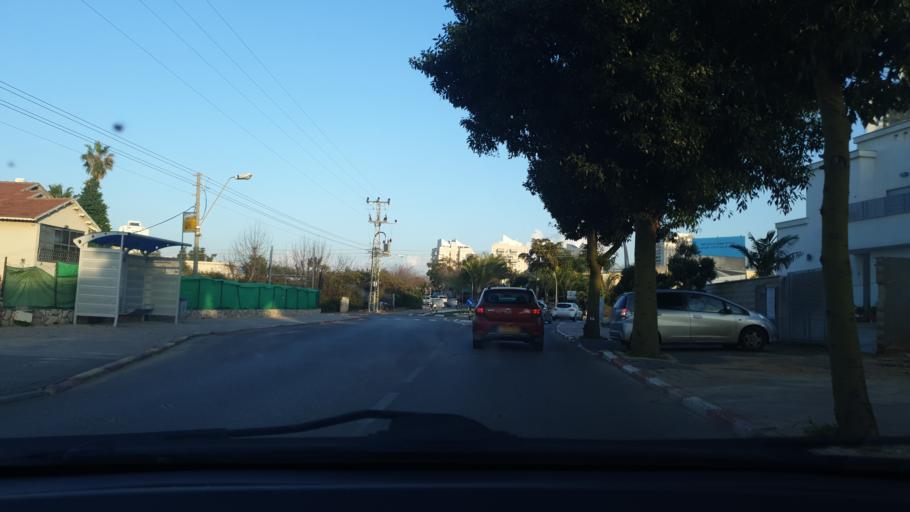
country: IL
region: Central District
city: Ramla
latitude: 31.9357
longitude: 34.8484
